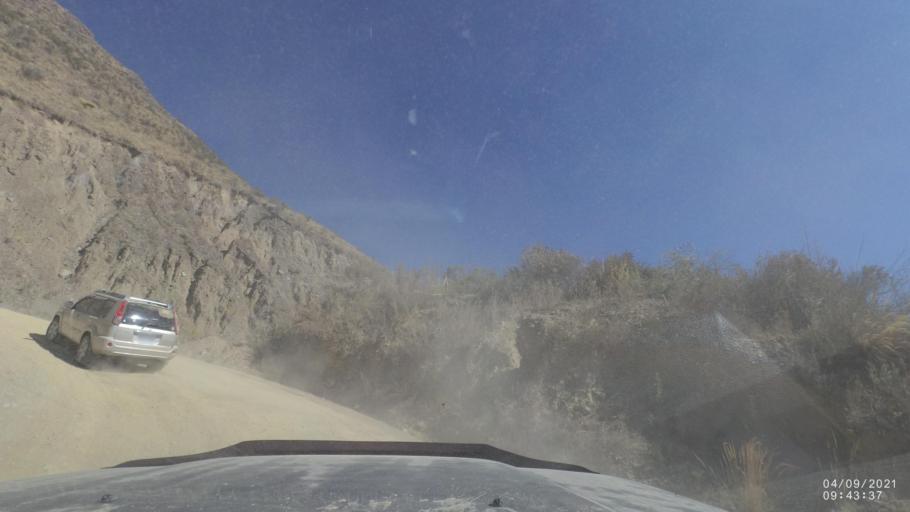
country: BO
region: Cochabamba
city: Sipe Sipe
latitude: -17.3388
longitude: -66.3908
